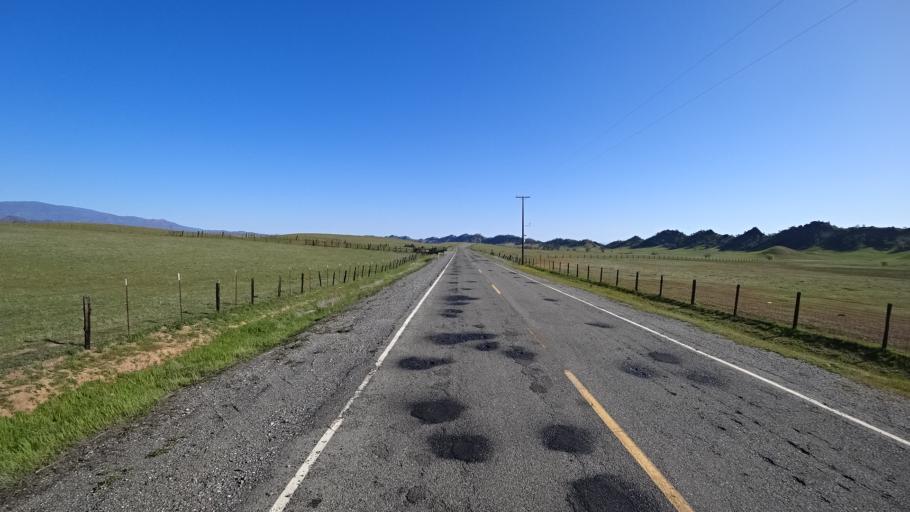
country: US
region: California
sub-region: Tehama County
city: Rancho Tehama Reserve
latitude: 39.7356
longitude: -122.5473
